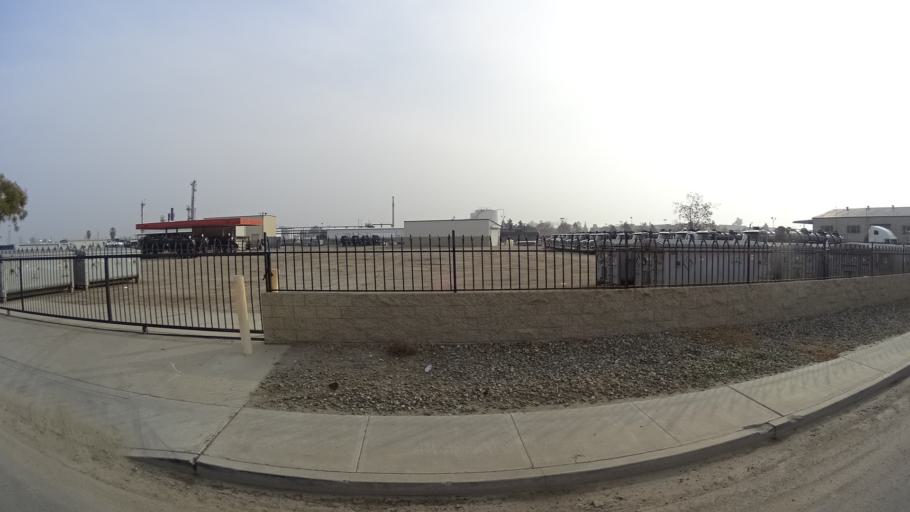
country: US
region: California
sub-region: Kern County
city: Bakersfield
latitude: 35.3862
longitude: -119.0521
